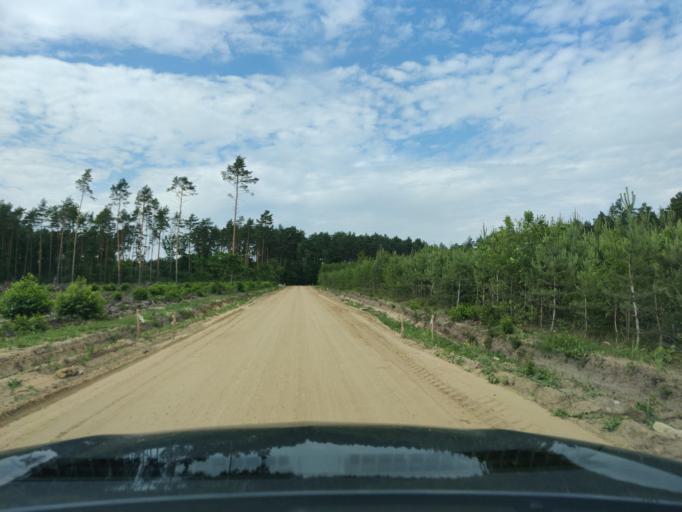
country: PL
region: Masovian Voivodeship
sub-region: Powiat pultuski
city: Pultusk
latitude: 52.7191
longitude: 21.1499
